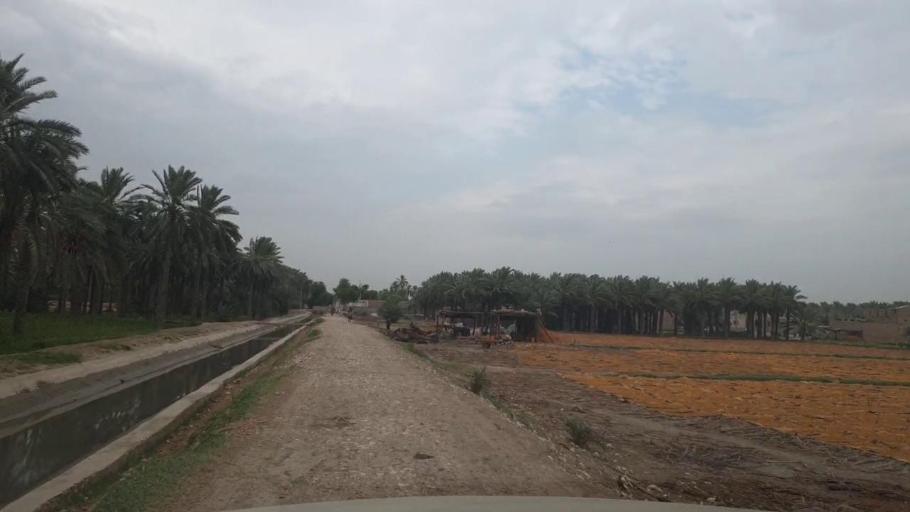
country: PK
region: Sindh
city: Sukkur
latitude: 27.6257
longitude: 68.8203
